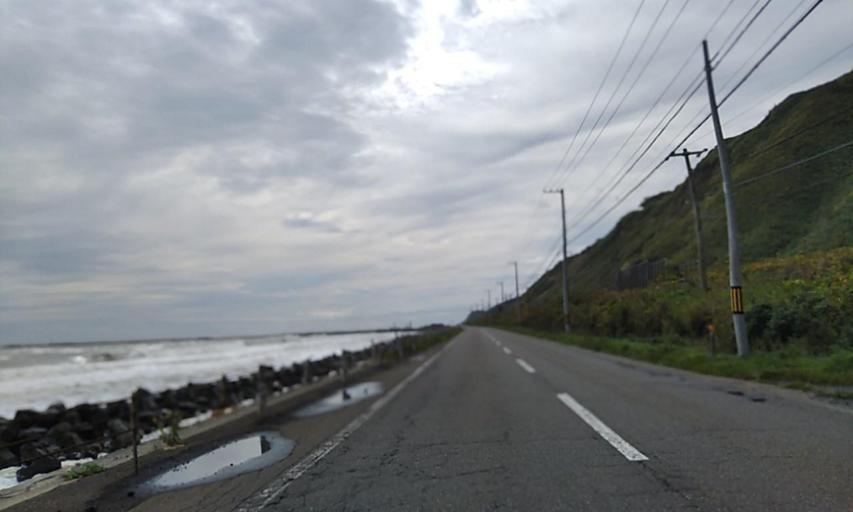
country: JP
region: Hokkaido
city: Kushiro
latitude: 42.8137
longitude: 143.8294
